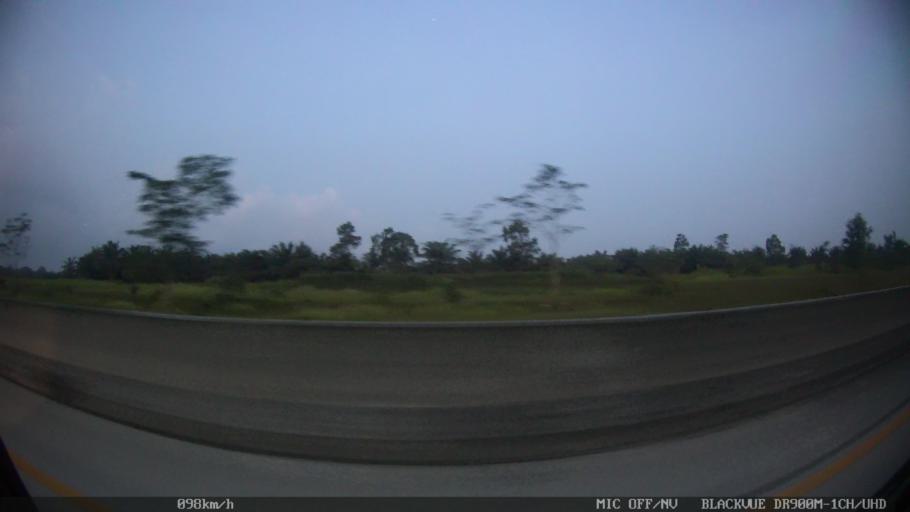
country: ID
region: Lampung
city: Sidorejo
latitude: -5.5481
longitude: 105.5243
